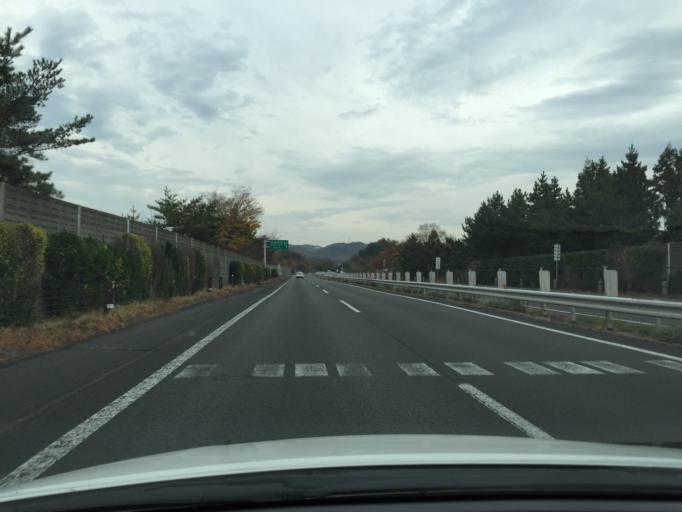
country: JP
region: Fukushima
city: Fukushima-shi
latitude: 37.7150
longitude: 140.4396
